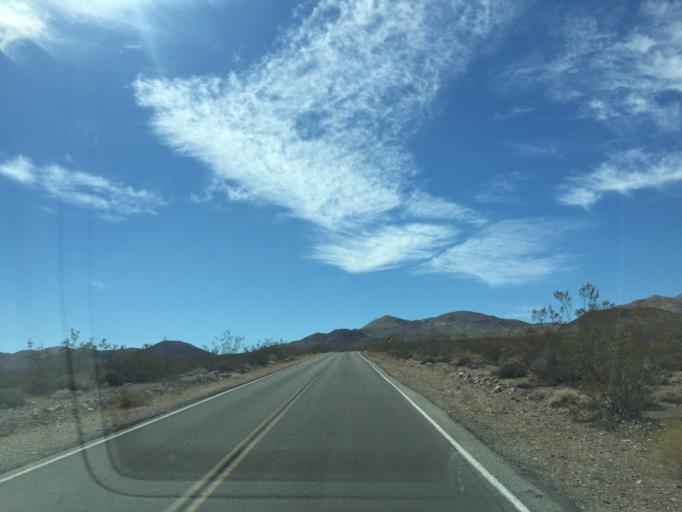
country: US
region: Nevada
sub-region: Nye County
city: Beatty
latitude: 36.2512
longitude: -116.6793
